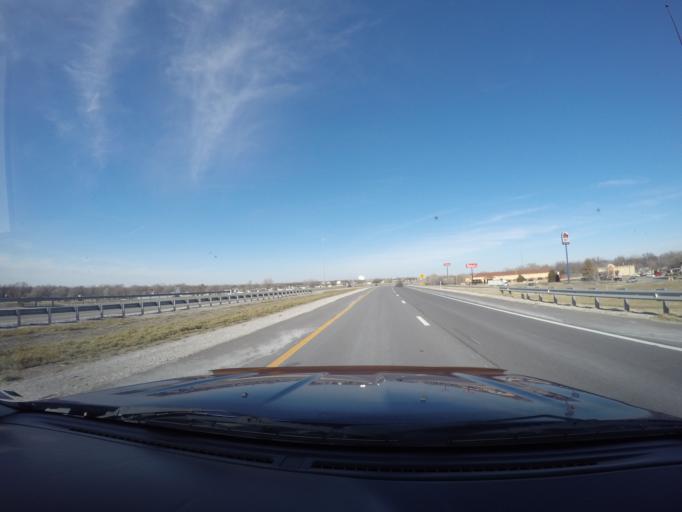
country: US
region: Kansas
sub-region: Sedgwick County
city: Park City
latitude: 37.7965
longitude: -97.3285
